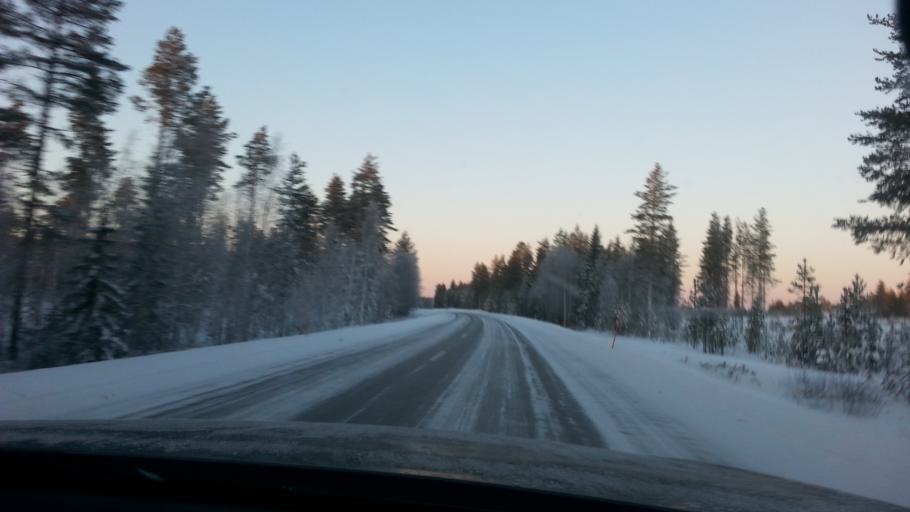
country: FI
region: Lapland
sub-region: Rovaniemi
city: Rovaniemi
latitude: 66.7758
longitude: 25.4564
